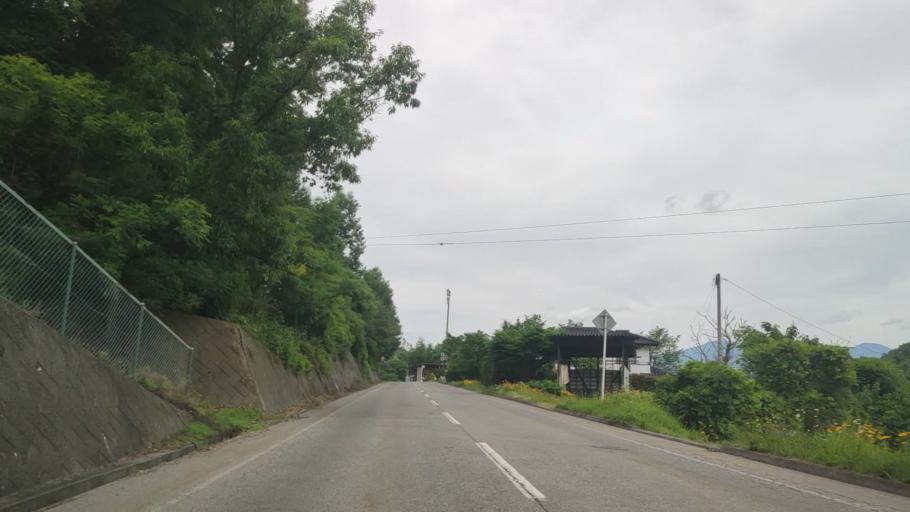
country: JP
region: Nagano
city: Kamimaruko
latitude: 36.3087
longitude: 138.3283
